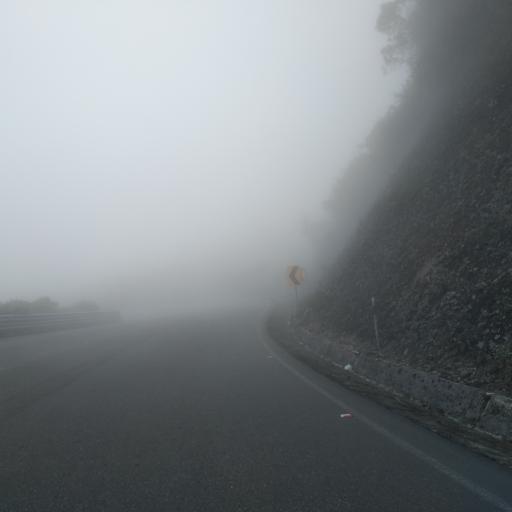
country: EC
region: Cotopaxi
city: La Mana
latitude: -0.9870
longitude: -78.9773
